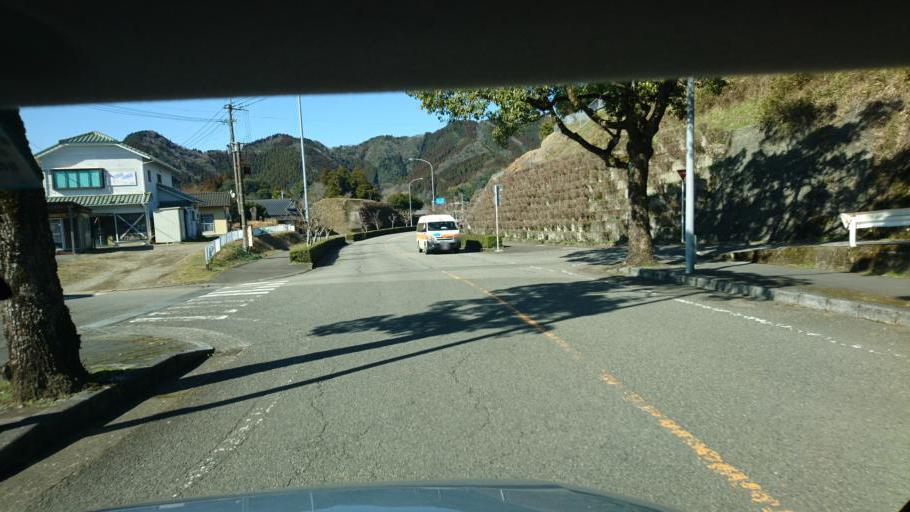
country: JP
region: Oita
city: Takedamachi
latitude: 32.7150
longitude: 131.3074
